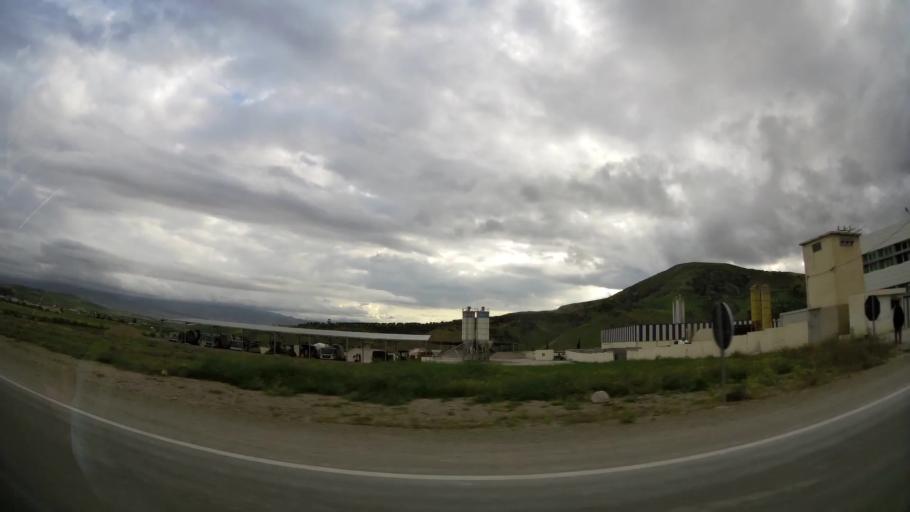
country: MA
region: Taza-Al Hoceima-Taounate
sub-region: Taza
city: Taza
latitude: 34.2797
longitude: -3.9570
